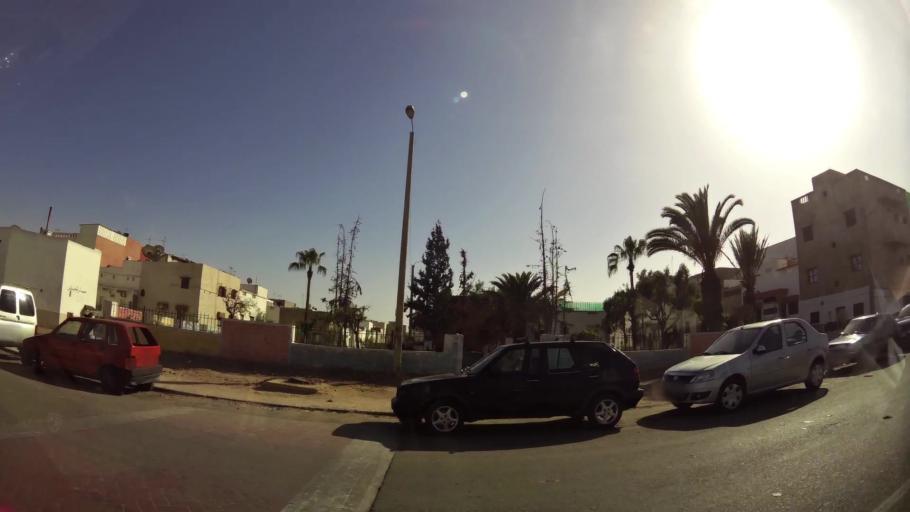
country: MA
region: Oued ed Dahab-Lagouira
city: Dakhla
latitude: 30.4192
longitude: -9.5702
